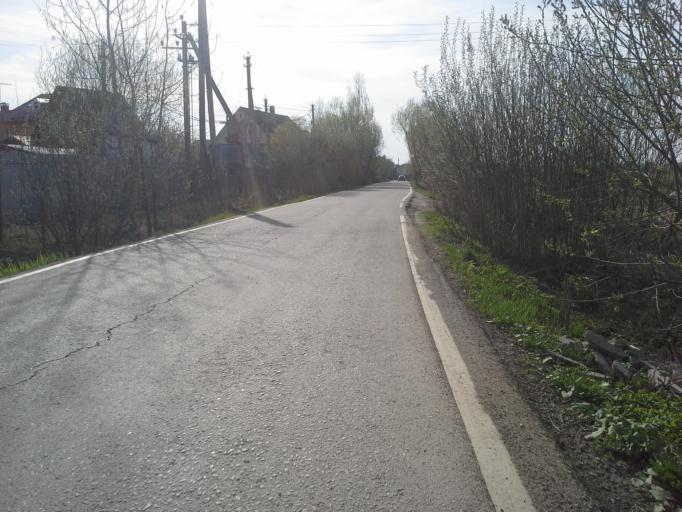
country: RU
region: Moskovskaya
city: Vatutinki
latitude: 55.4601
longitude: 37.3875
